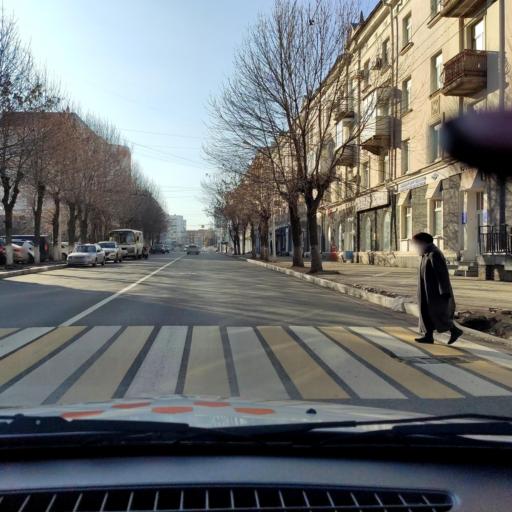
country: RU
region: Bashkortostan
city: Ufa
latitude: 54.7383
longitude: 55.9468
